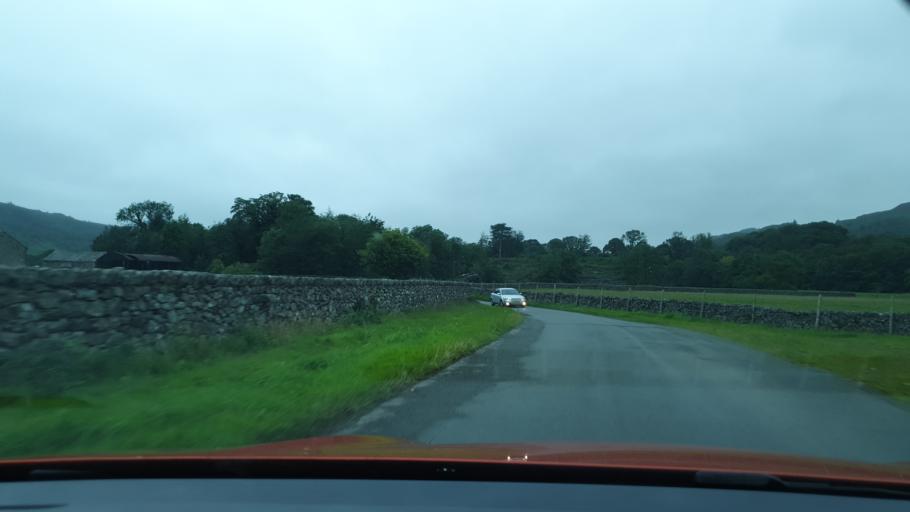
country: GB
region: England
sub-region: Cumbria
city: Seascale
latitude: 54.3832
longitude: -3.3143
